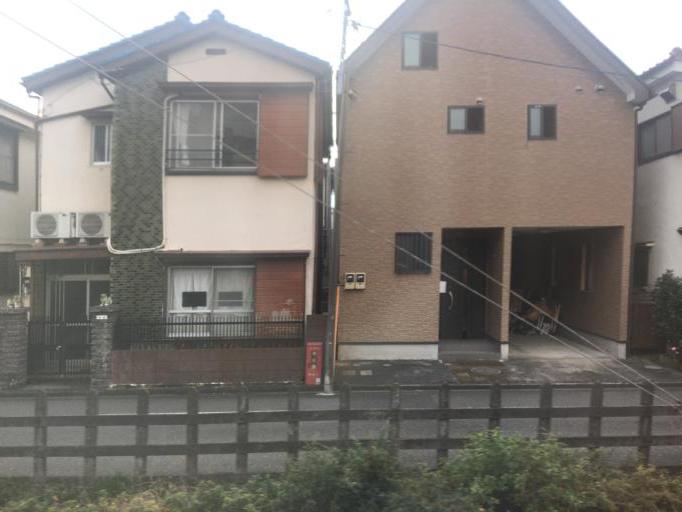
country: JP
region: Tokyo
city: Hino
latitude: 35.7076
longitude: 139.3806
